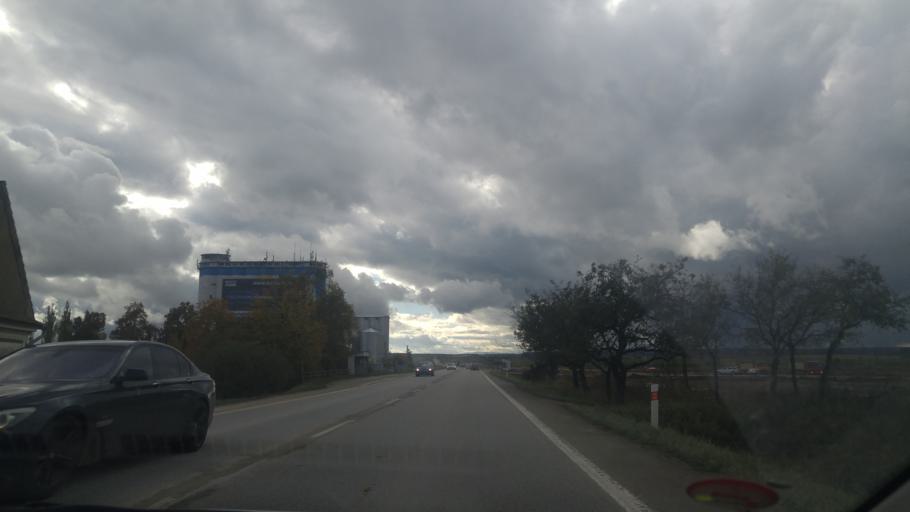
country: CZ
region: Jihocesky
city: Dolni Bukovsko
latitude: 49.1482
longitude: 14.6274
